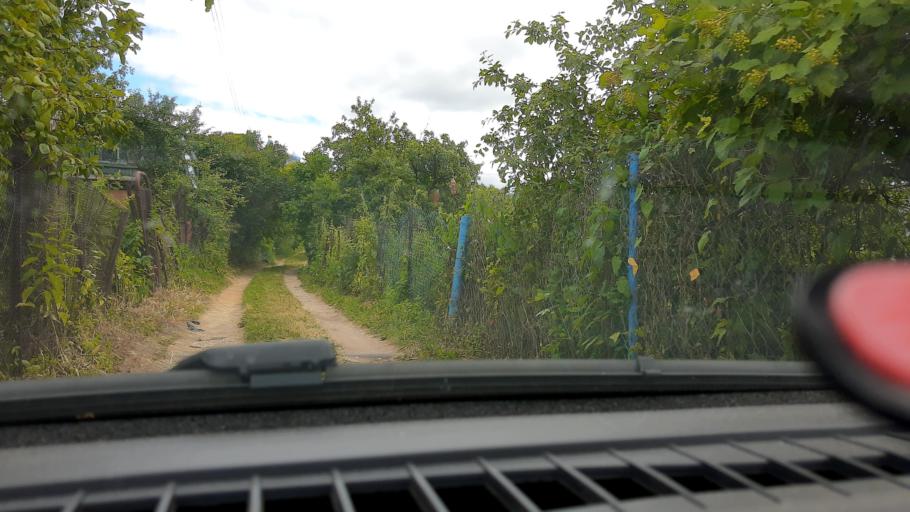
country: RU
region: Nizjnij Novgorod
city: Kstovo
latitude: 56.1425
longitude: 44.1722
